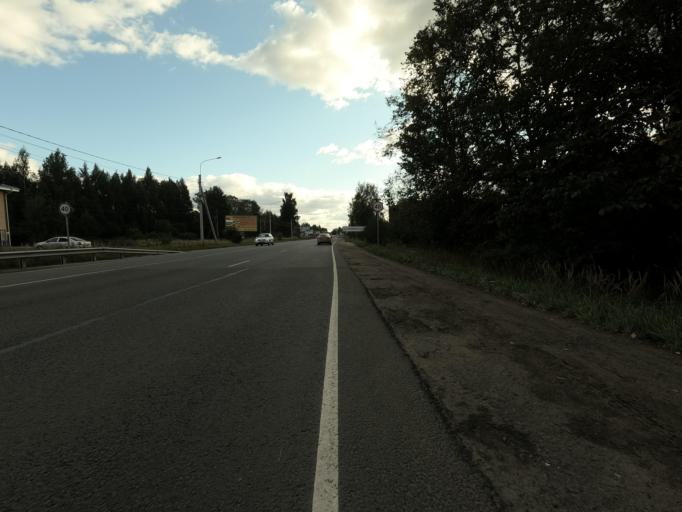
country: RU
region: Leningrad
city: Vsevolozhsk
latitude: 59.9890
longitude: 30.6570
